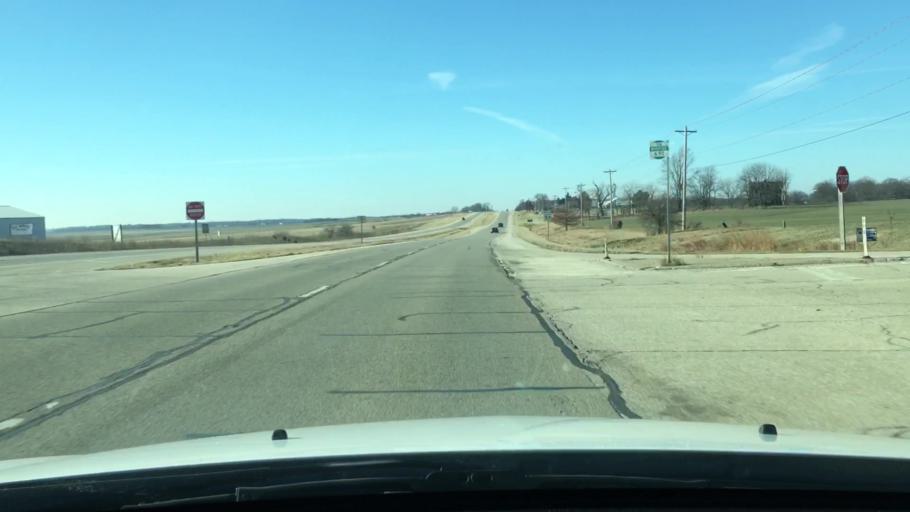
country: US
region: Illinois
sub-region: Woodford County
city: Metamora
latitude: 40.7845
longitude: -89.3890
